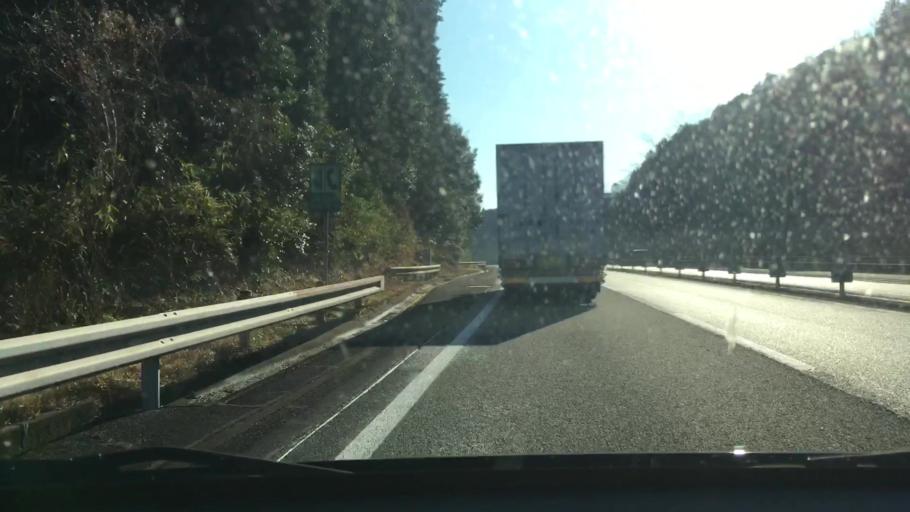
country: JP
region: Kagoshima
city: Kajiki
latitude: 31.8912
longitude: 130.6983
